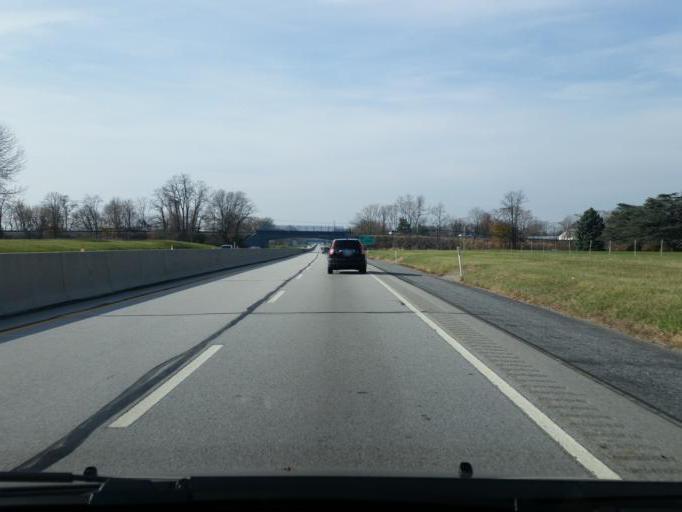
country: US
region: Pennsylvania
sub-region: Cumberland County
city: Mechanicsburg
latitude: 40.1969
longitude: -76.9916
